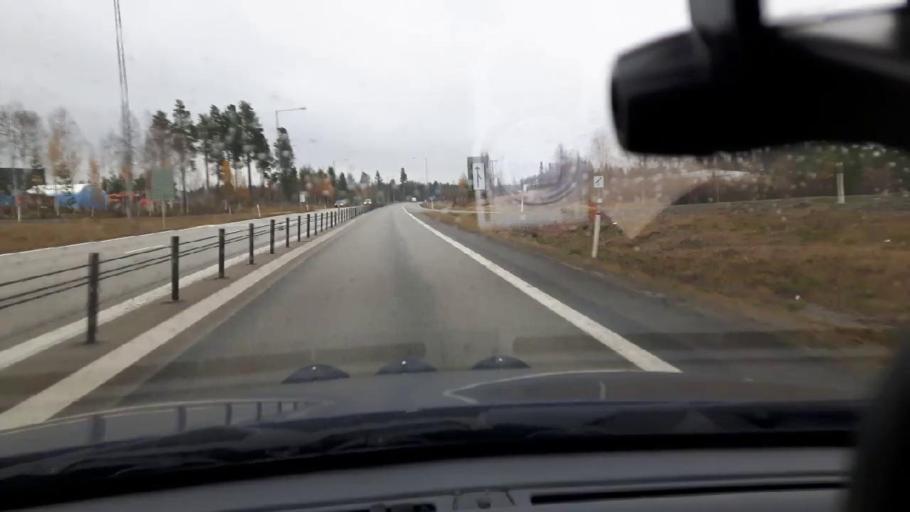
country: SE
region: Jaemtland
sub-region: OEstersunds Kommun
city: Ostersund
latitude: 63.1629
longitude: 14.7435
